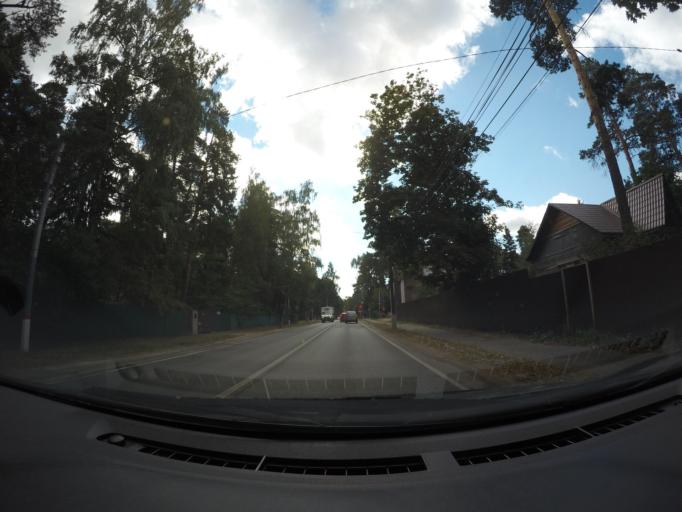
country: RU
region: Moskovskaya
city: Il'inskiy
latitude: 55.6234
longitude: 38.1146
